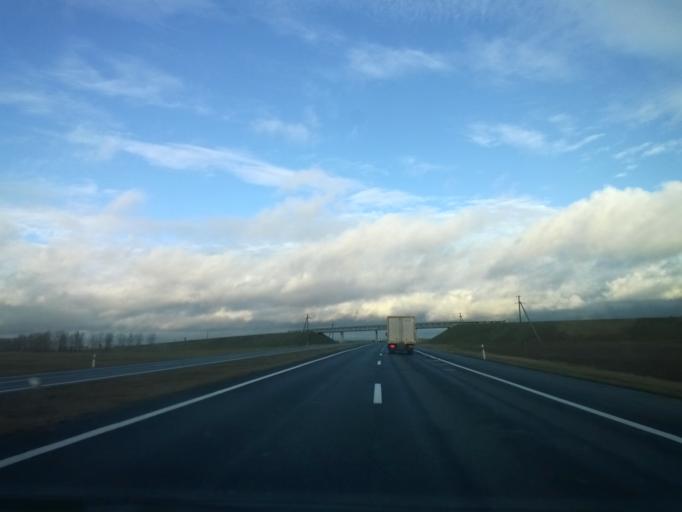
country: BY
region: Brest
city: Haradzishcha
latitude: 53.2340
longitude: 26.1745
